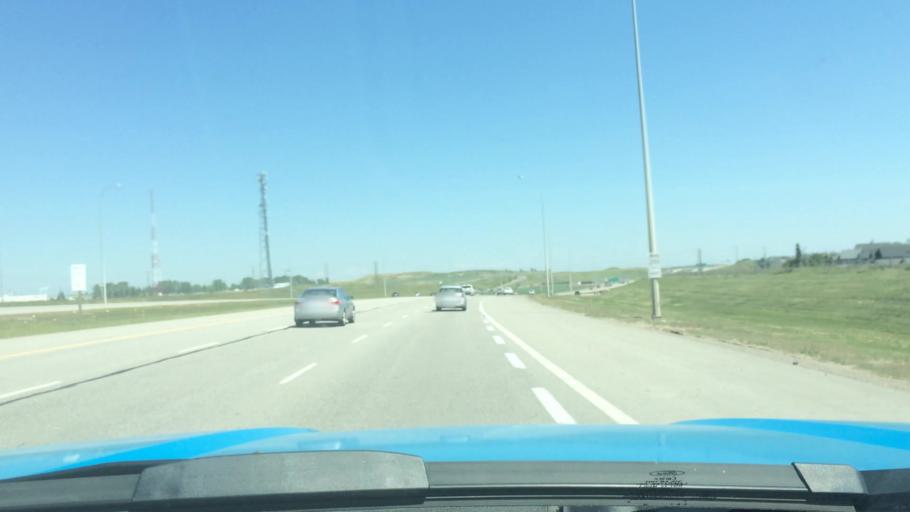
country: CA
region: Alberta
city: Calgary
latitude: 51.1495
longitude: -114.1940
